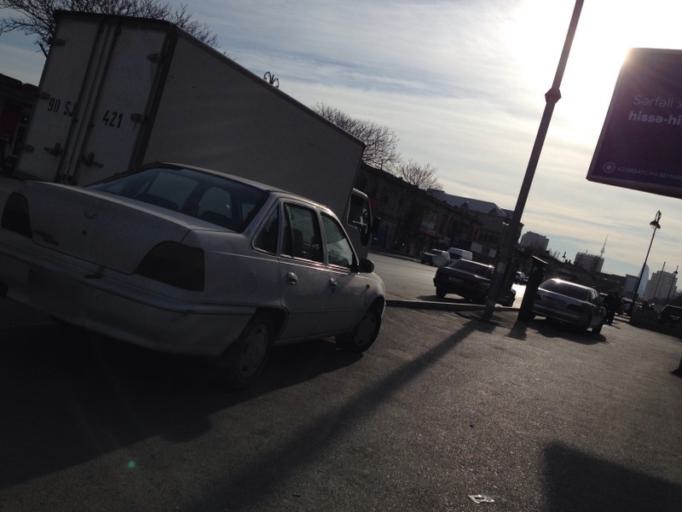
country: AZ
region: Baki
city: Baku
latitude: 40.3864
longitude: 49.8557
